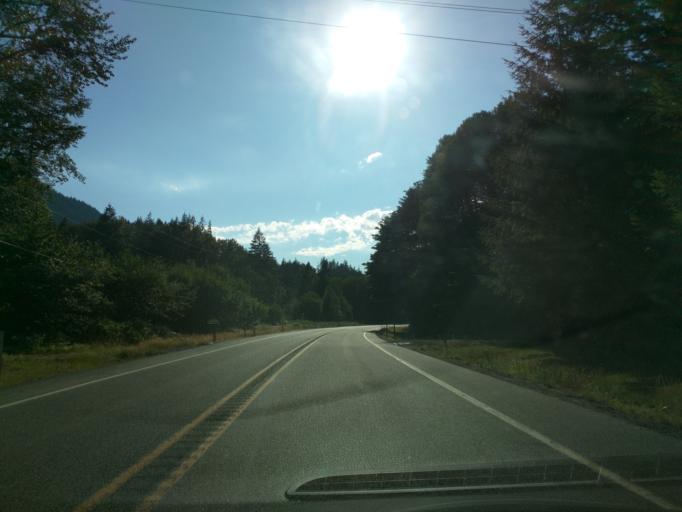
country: US
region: Washington
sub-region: Snohomish County
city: Darrington
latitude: 48.2687
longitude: -121.7238
